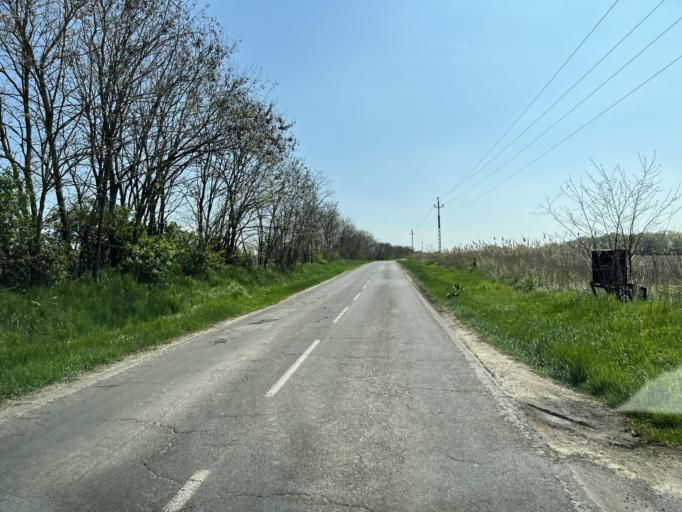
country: HU
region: Pest
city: Ocsa
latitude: 47.3028
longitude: 19.1973
